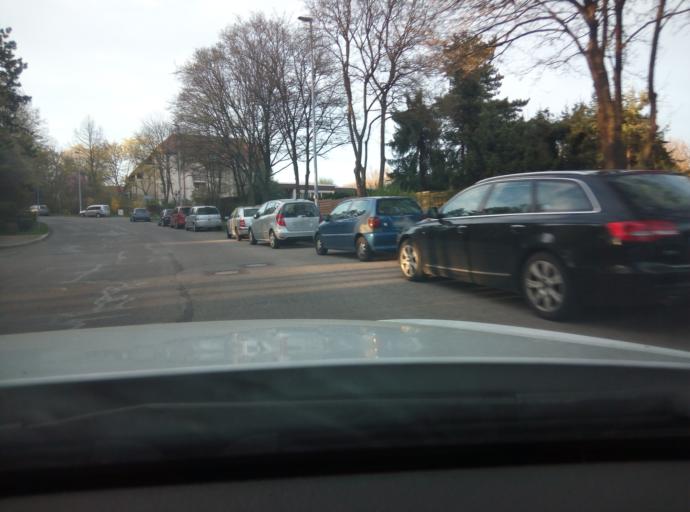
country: DE
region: Baden-Wuerttemberg
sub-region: Tuebingen Region
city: Tuebingen
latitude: 48.5433
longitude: 9.0649
